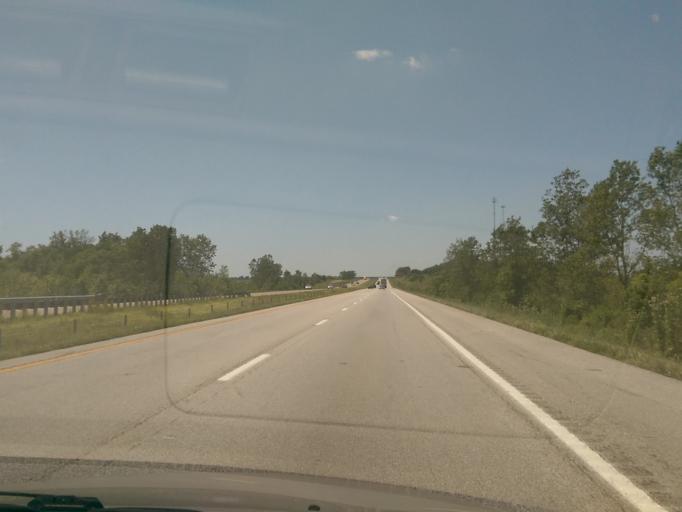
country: US
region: Missouri
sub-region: Cooper County
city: Boonville
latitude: 38.9349
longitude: -92.9020
